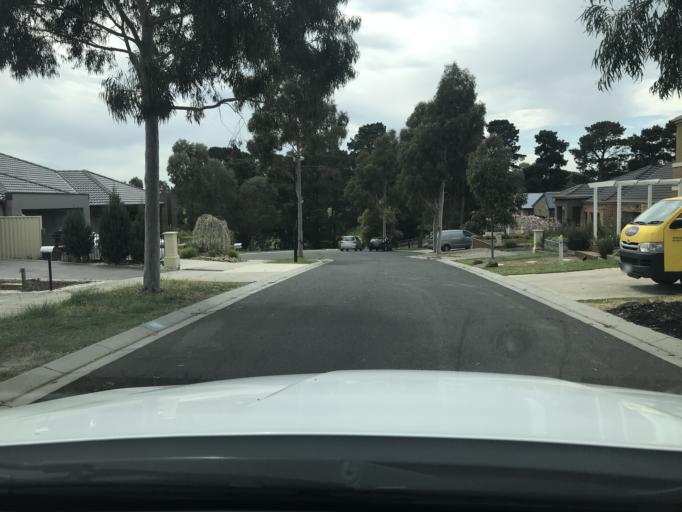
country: AU
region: Victoria
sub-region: Hume
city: Roxburgh Park
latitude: -37.6006
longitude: 144.9159
